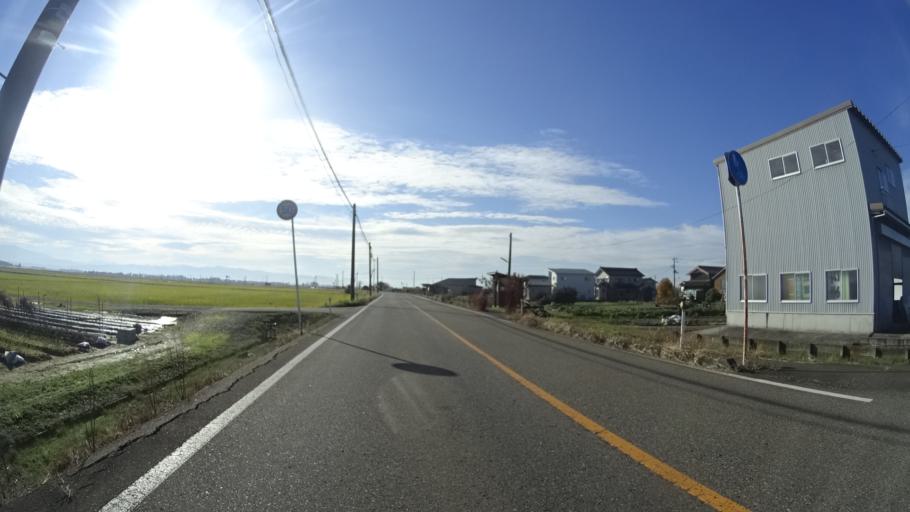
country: JP
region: Niigata
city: Mitsuke
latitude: 37.5721
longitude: 138.8415
